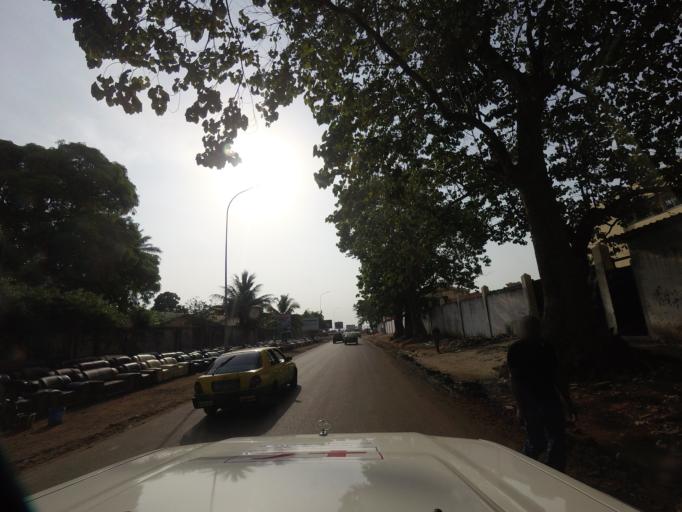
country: GN
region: Conakry
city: Camayenne
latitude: 9.5137
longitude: -13.6989
